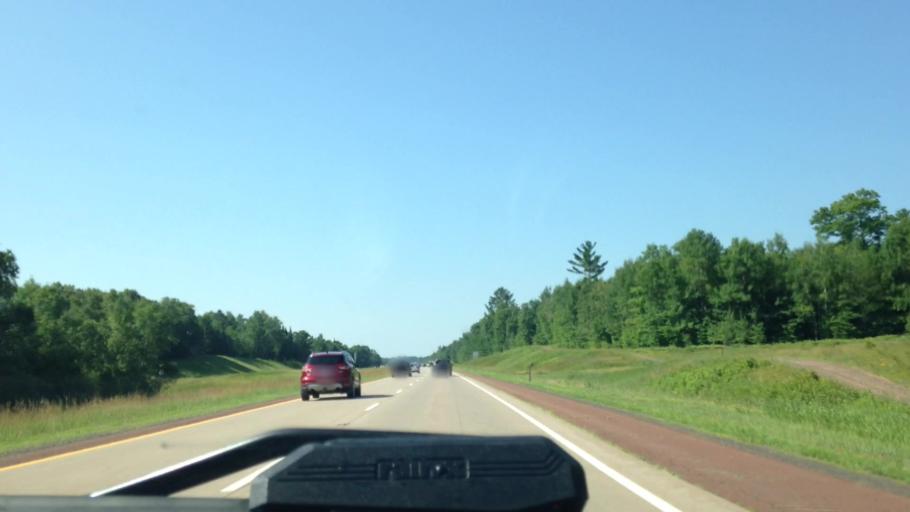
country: US
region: Wisconsin
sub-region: Douglas County
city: Lake Nebagamon
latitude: 46.3807
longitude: -91.8235
